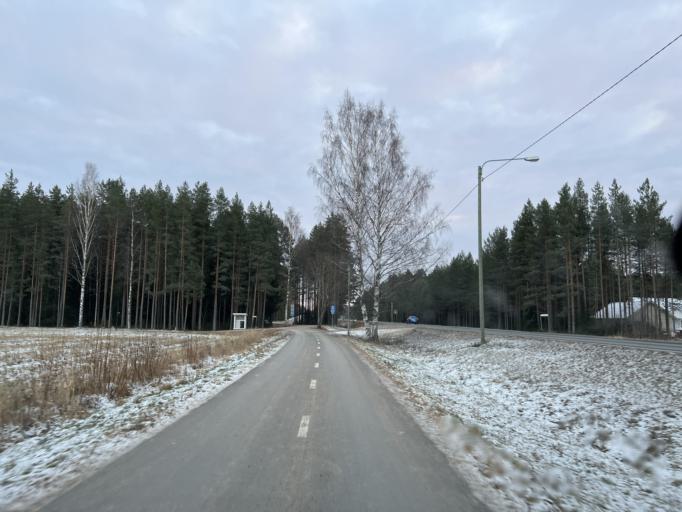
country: FI
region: Northern Ostrobothnia
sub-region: Oulu
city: Muhos
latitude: 64.8775
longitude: 25.8545
